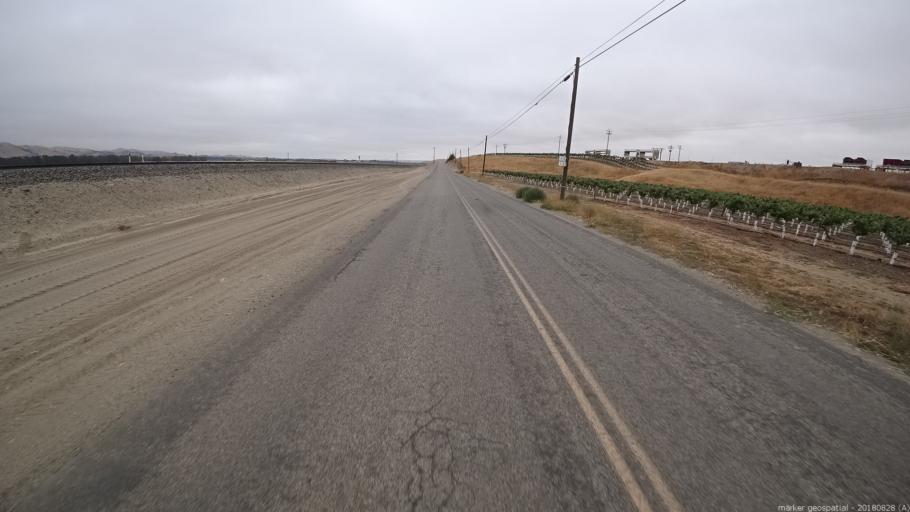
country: US
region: California
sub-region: San Luis Obispo County
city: Lake Nacimiento
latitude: 35.9862
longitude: -120.8791
